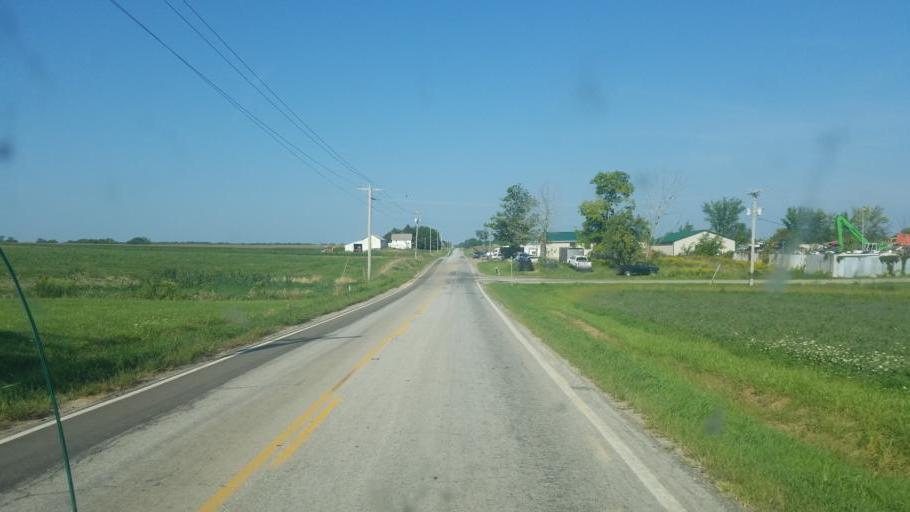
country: US
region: Ohio
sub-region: Lorain County
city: Wellington
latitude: 41.1003
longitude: -82.1417
